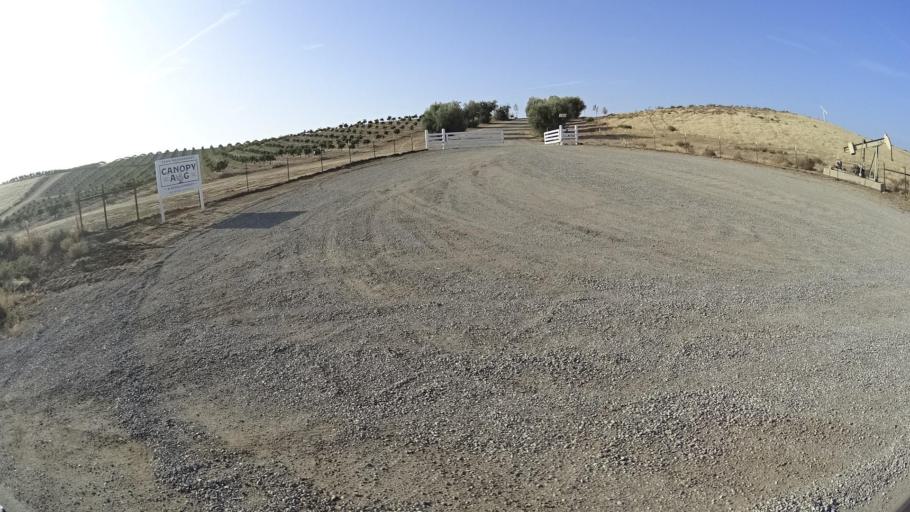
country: US
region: California
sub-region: Tulare County
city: Richgrove
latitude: 35.6437
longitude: -119.0507
